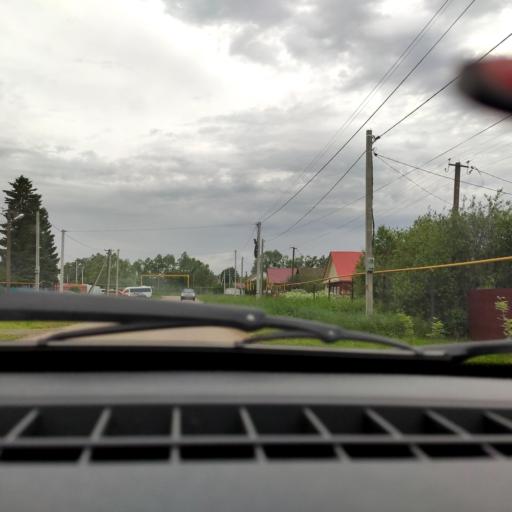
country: RU
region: Bashkortostan
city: Avdon
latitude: 54.6498
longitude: 55.7817
